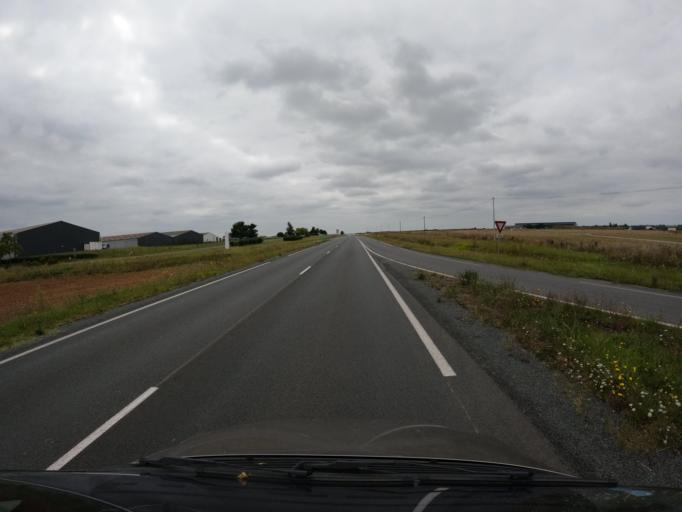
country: FR
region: Pays de la Loire
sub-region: Departement de la Vendee
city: Fontenay-le-Comte
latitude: 46.4436
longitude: -0.7868
